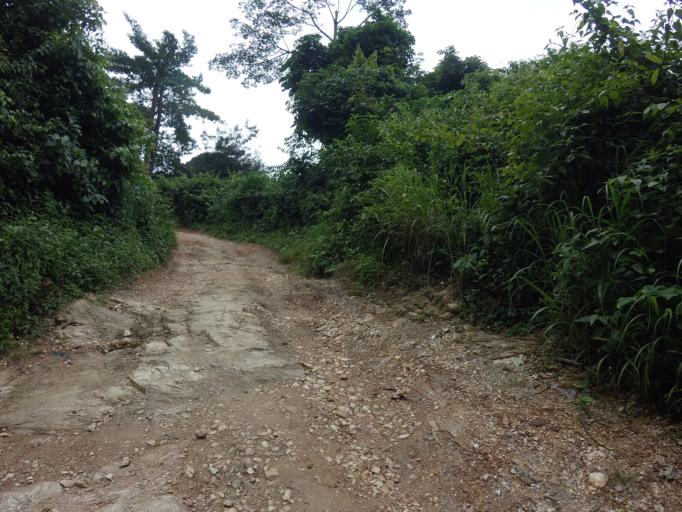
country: TG
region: Plateaux
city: Kpalime
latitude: 6.8572
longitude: 0.4418
